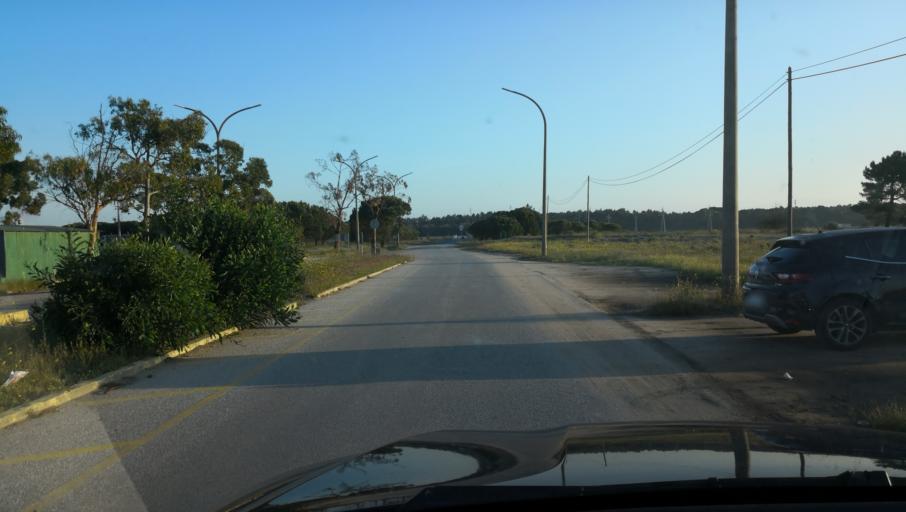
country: PT
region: Setubal
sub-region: Setubal
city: Setubal
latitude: 38.4819
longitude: -8.7930
